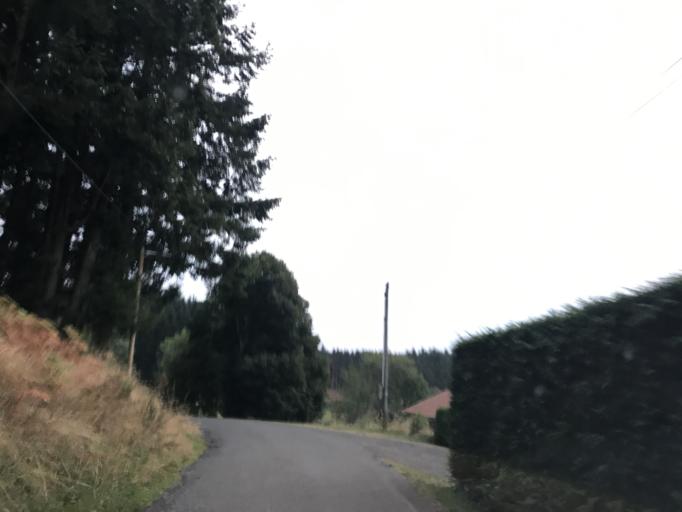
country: FR
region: Auvergne
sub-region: Departement du Puy-de-Dome
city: La Monnerie-le-Montel
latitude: 45.8462
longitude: 3.5978
